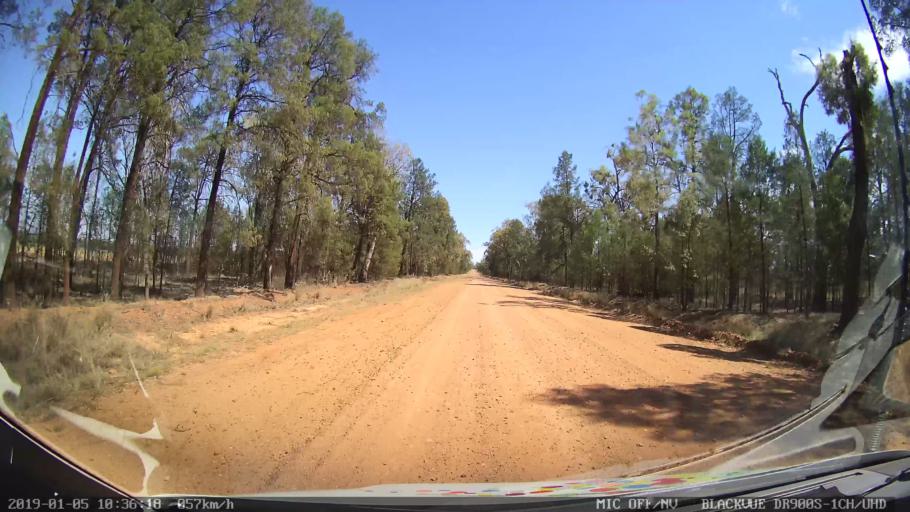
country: AU
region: New South Wales
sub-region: Gilgandra
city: Gilgandra
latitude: -31.4831
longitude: 148.9255
